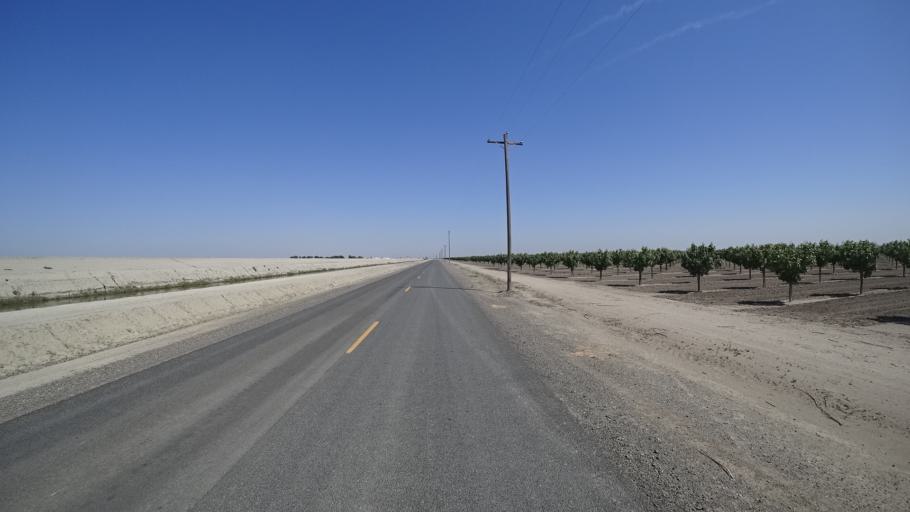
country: US
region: California
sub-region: Kings County
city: Corcoran
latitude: 36.0426
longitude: -119.5361
